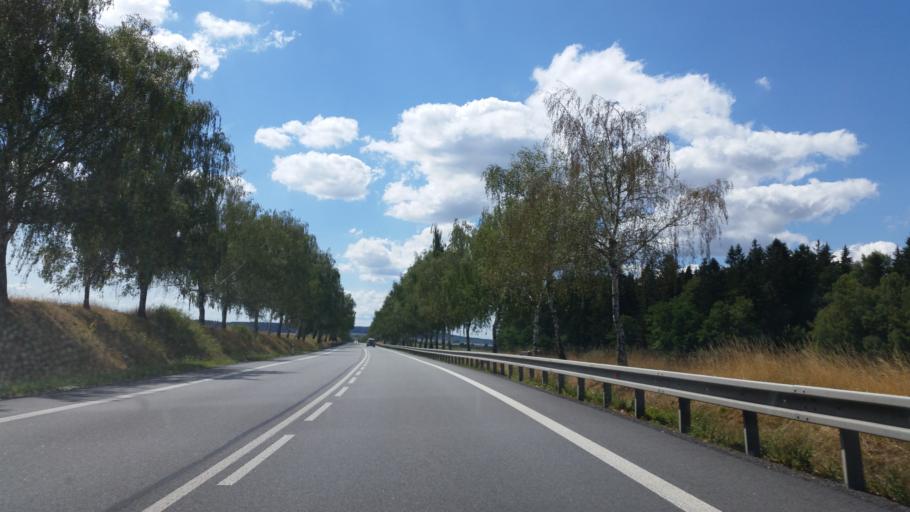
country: CZ
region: Vysocina
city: Nova Cerekev
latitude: 49.4281
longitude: 15.0694
